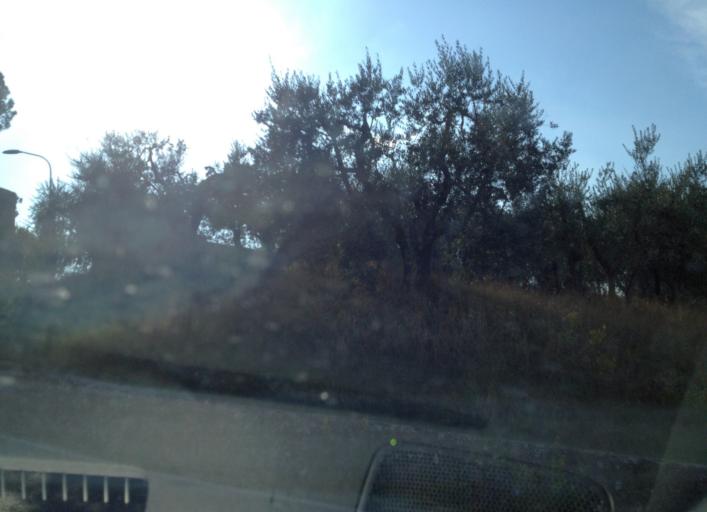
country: IT
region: Tuscany
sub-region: Provincia di Siena
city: San Gimignano
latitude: 43.4718
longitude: 11.0415
